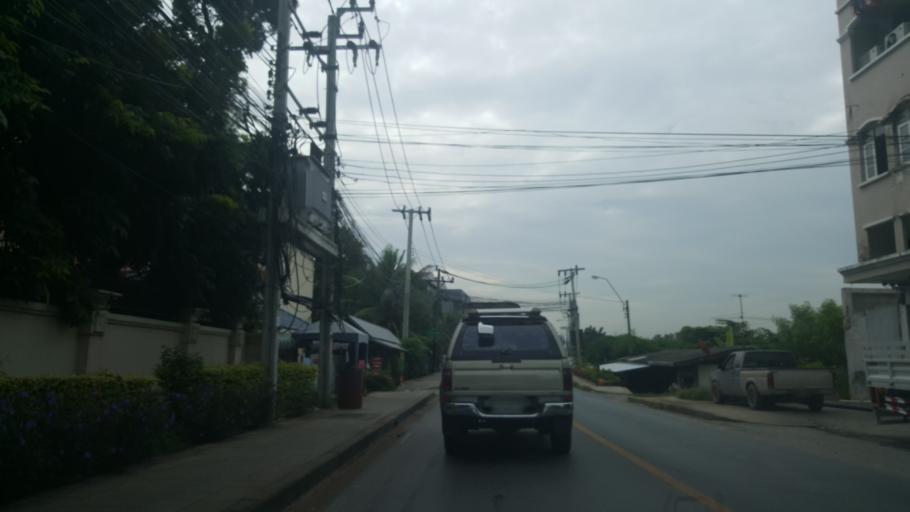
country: TH
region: Bangkok
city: Bang Bon
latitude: 13.6745
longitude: 100.4020
